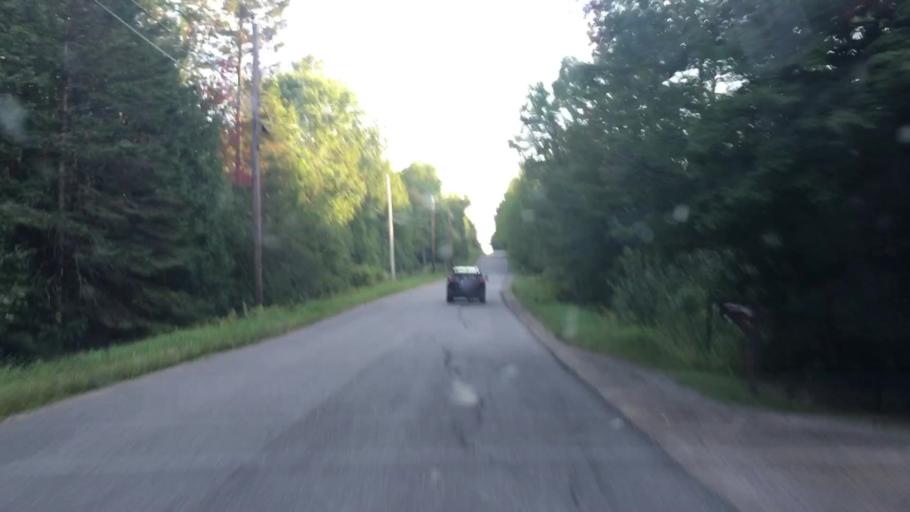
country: US
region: Maine
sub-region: Waldo County
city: Winterport
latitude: 44.6821
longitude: -68.9119
